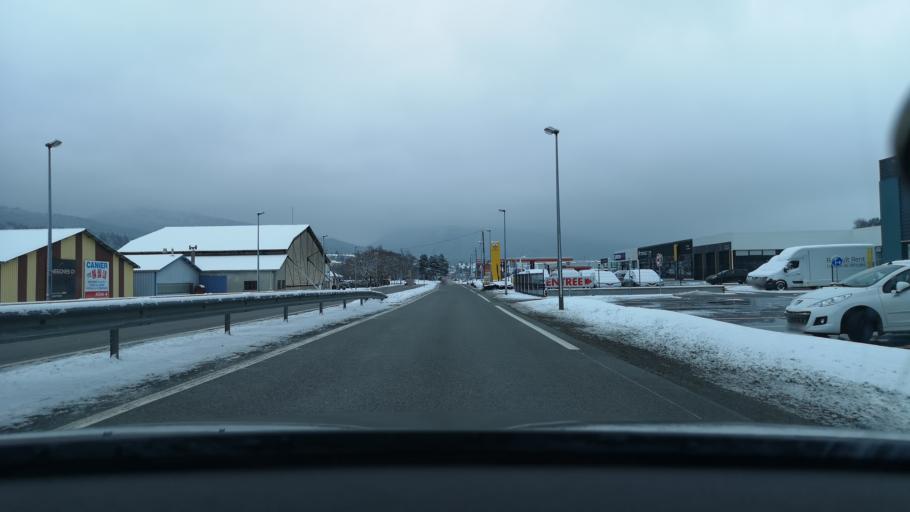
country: FR
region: Rhone-Alpes
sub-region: Departement de l'Ain
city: Oyonnax
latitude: 46.2777
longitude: 5.6606
